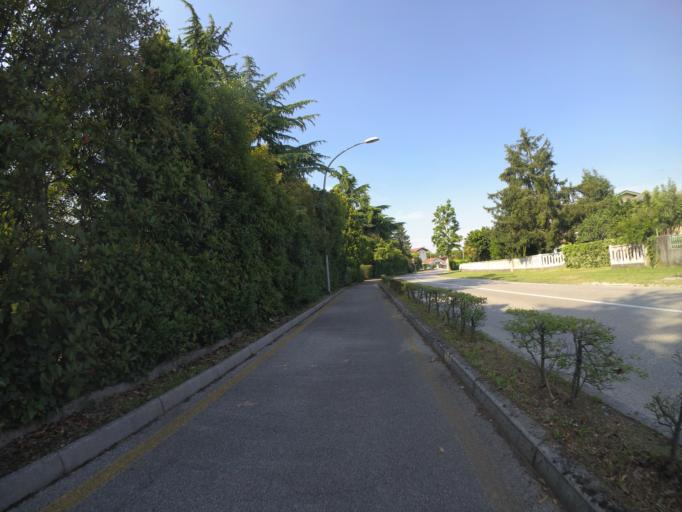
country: IT
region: Friuli Venezia Giulia
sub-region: Provincia di Udine
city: Camino al Tagliamento
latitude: 45.9438
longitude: 12.9645
